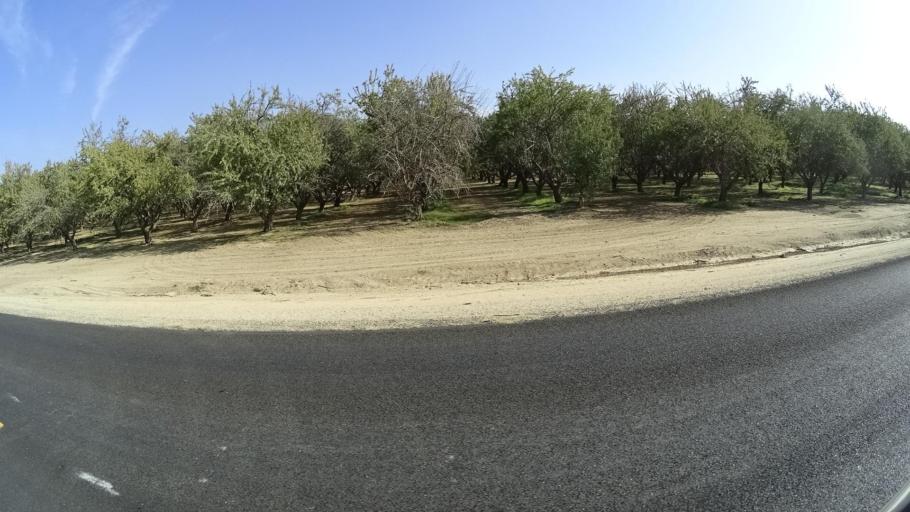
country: US
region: California
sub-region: Kern County
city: Shafter
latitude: 35.5274
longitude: -119.1516
